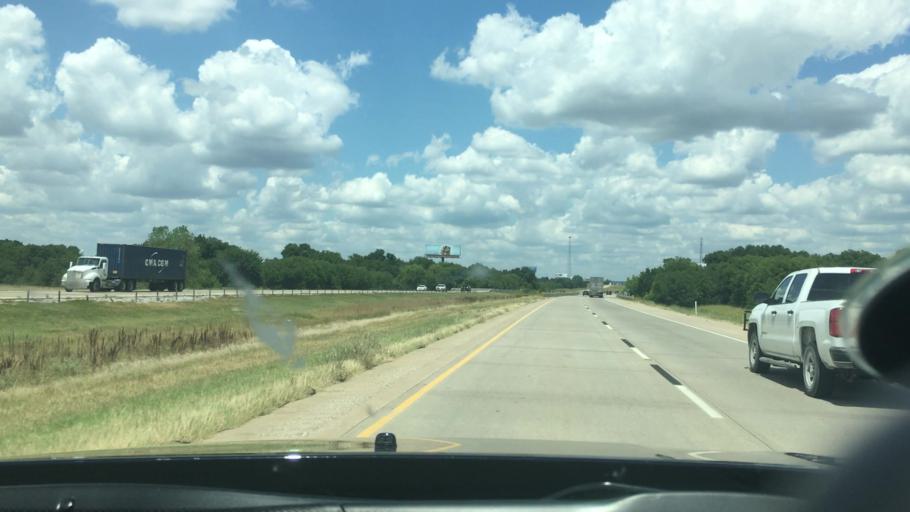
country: US
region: Oklahoma
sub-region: Carter County
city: Ardmore
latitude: 34.2607
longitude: -97.1647
